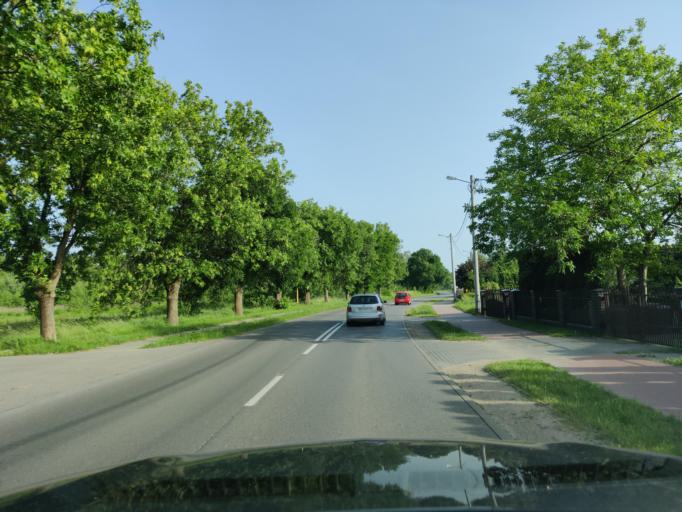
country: PL
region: Masovian Voivodeship
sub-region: Powiat wyszkowski
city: Wyszkow
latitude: 52.6428
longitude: 21.4526
